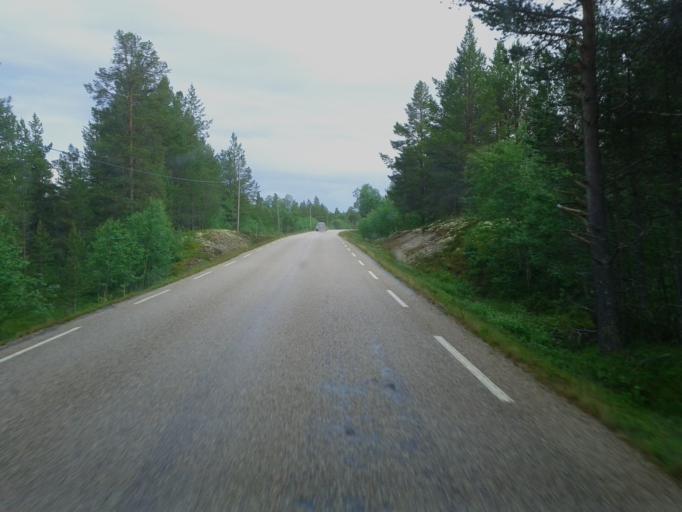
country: NO
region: Hedmark
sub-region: Engerdal
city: Engerdal
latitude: 62.0679
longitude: 11.6779
